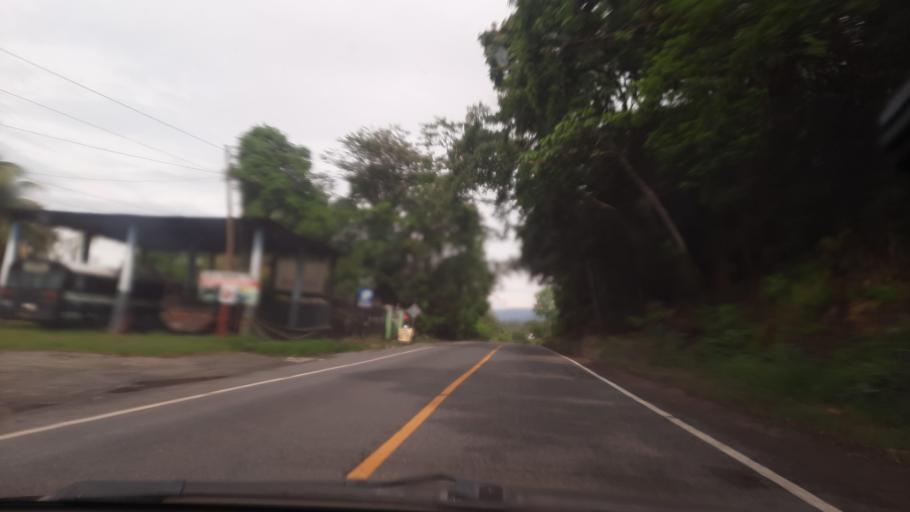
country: GT
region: Izabal
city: Morales
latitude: 15.5230
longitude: -88.7887
